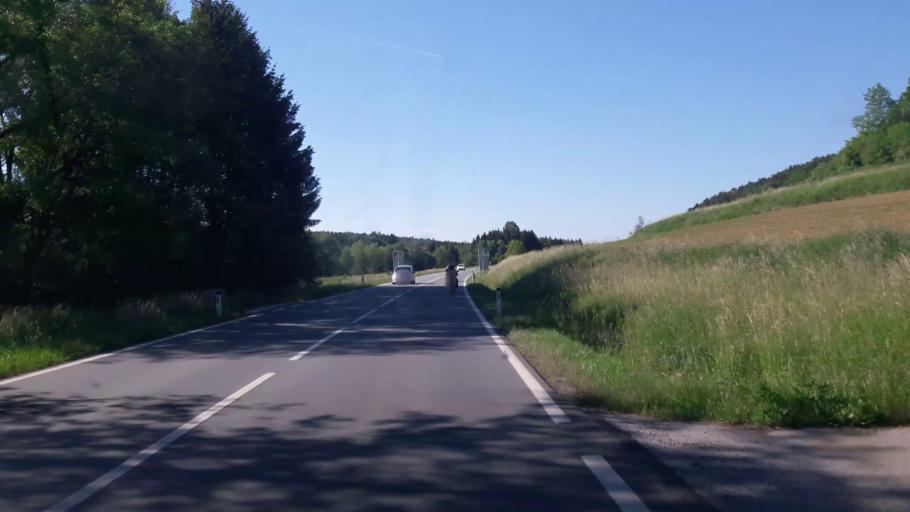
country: AT
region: Burgenland
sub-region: Politischer Bezirk Gussing
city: Ollersdorf im Burgenland
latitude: 47.1914
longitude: 16.1622
